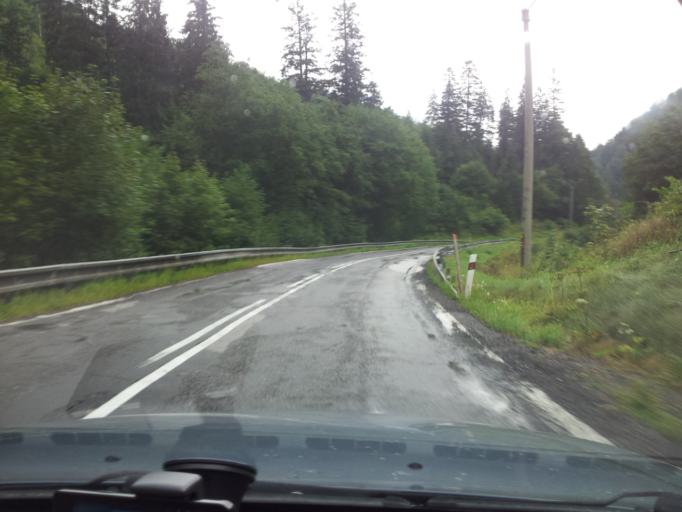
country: SK
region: Banskobystricky
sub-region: Okres Banska Bystrica
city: Brezno
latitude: 48.8869
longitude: 19.6716
